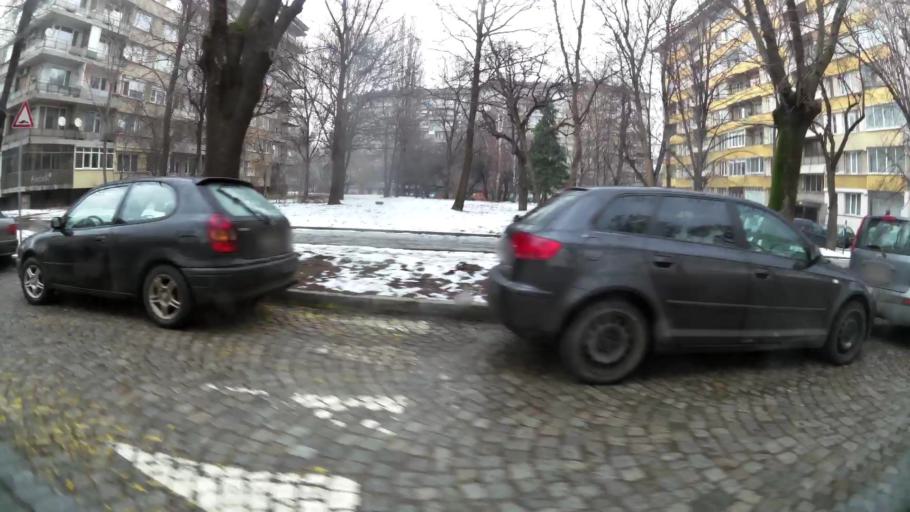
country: BG
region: Sofia-Capital
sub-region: Stolichna Obshtina
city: Sofia
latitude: 42.6823
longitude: 23.2998
